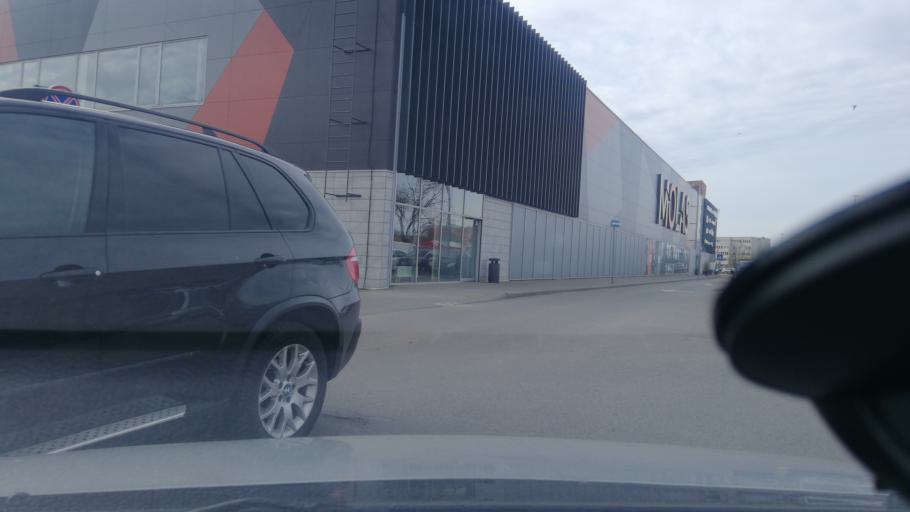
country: LT
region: Klaipedos apskritis
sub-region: Klaipeda
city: Klaipeda
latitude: 55.6665
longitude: 21.1773
